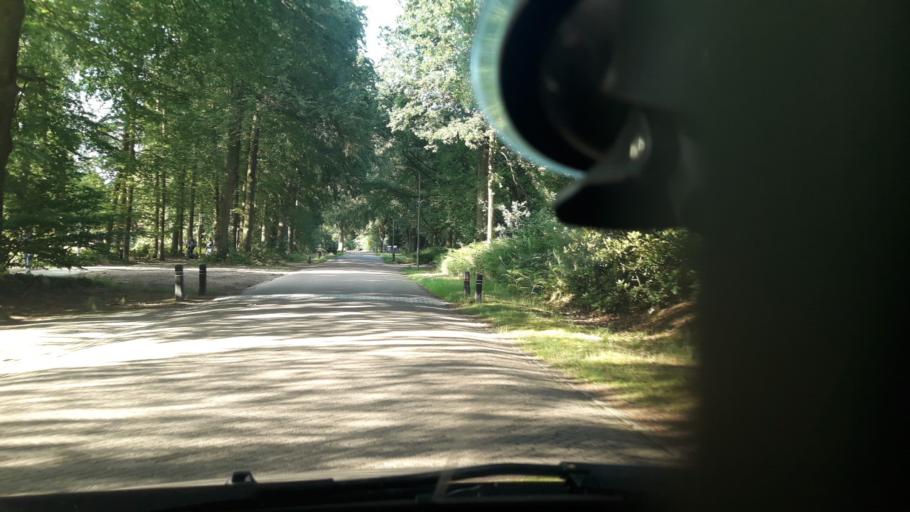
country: NL
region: Gelderland
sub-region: Gemeente Ermelo
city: Horst
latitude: 52.3147
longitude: 5.5968
